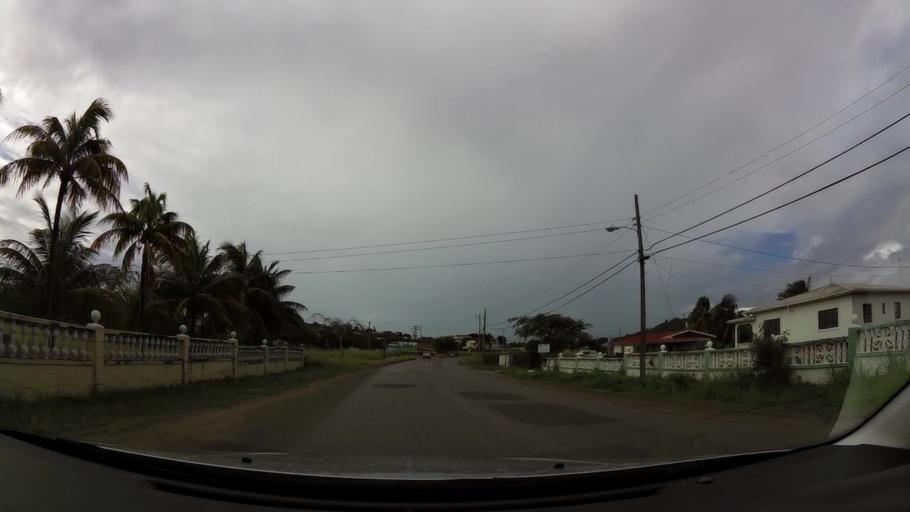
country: AG
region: Saint John
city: Potters Village
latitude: 17.0911
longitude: -61.8166
